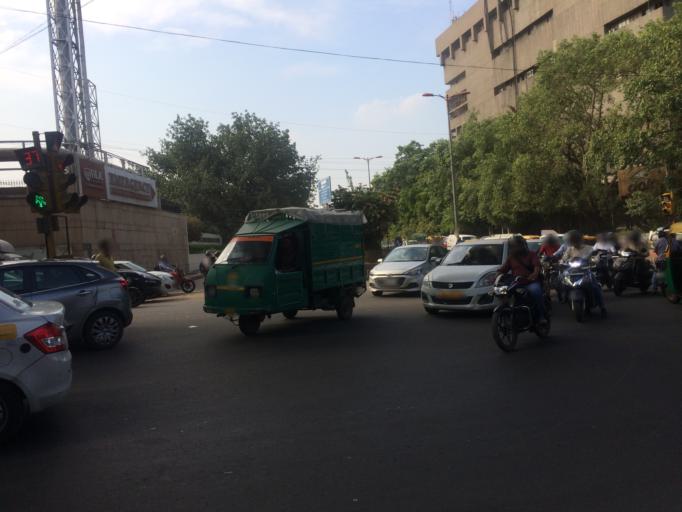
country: IN
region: NCT
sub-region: Central Delhi
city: Karol Bagh
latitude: 28.6428
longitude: 77.1809
